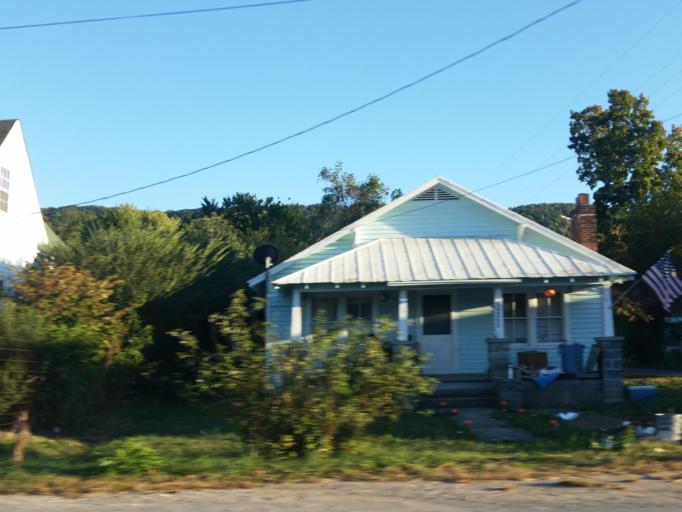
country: US
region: Tennessee
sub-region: Grainger County
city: Rutledge
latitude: 36.2929
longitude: -83.5951
